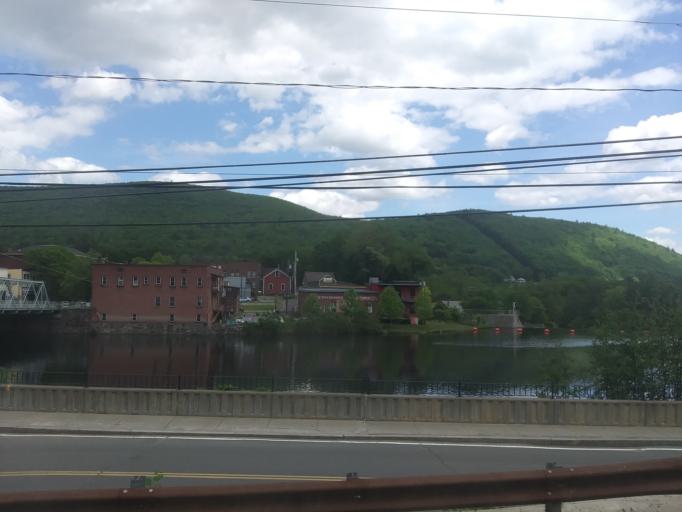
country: US
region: Massachusetts
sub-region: Franklin County
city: Shelburne Falls
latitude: 42.6032
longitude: -72.7415
